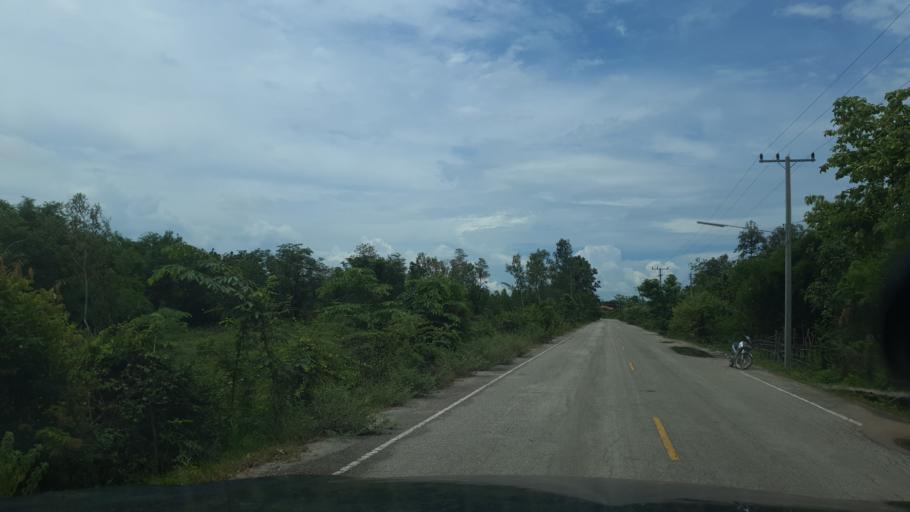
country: TH
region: Lampang
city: Ko Kha
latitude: 18.2447
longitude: 99.3692
